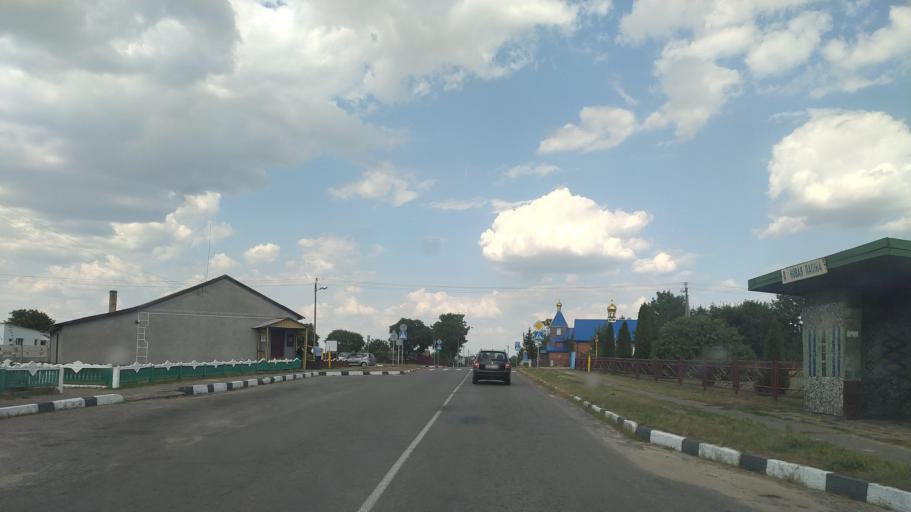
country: BY
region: Brest
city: Drahichyn
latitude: 52.1157
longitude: 25.1161
